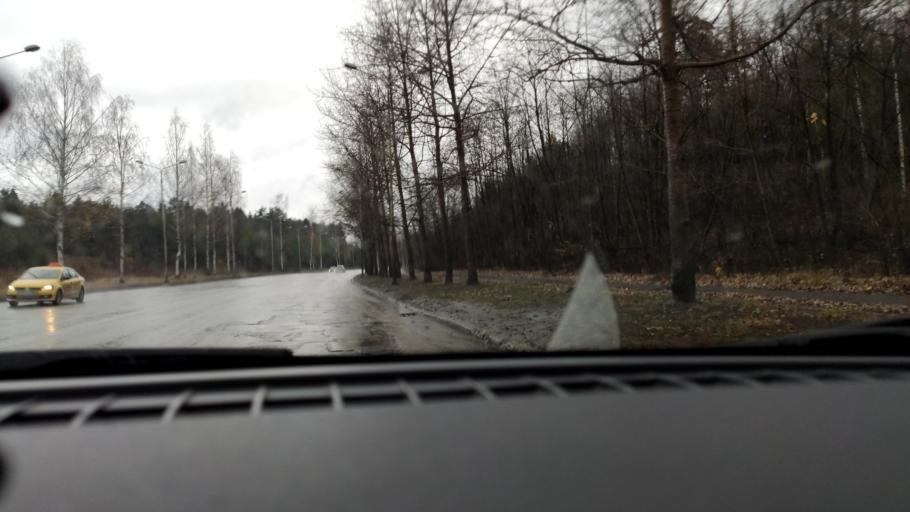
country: RU
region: Perm
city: Perm
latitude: 58.0729
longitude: 56.3678
